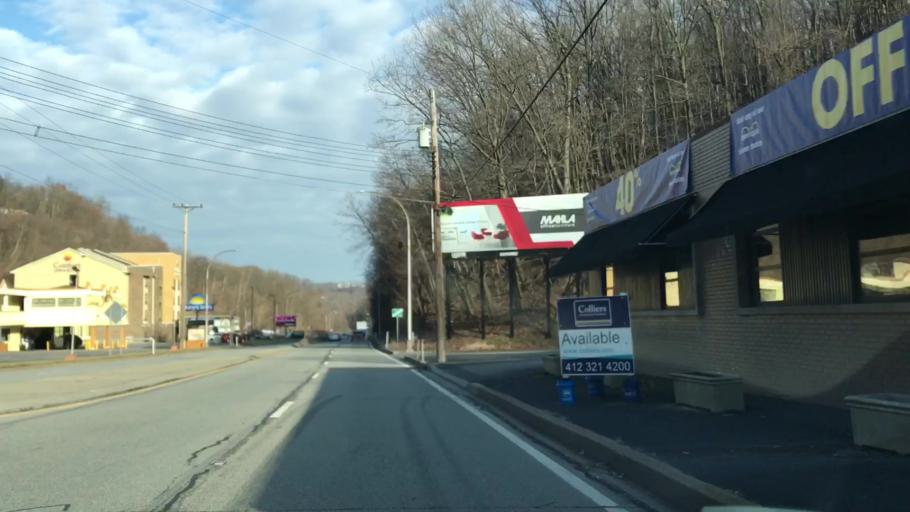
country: US
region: Pennsylvania
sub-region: Allegheny County
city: Green Tree
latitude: 40.4181
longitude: -80.0301
